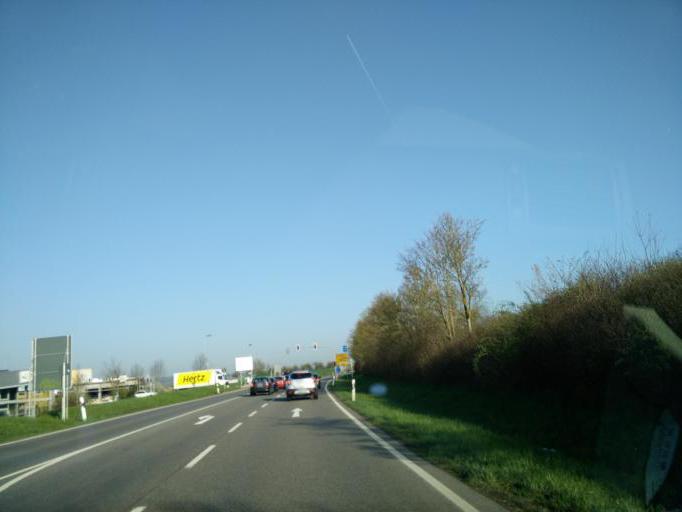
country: DE
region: Baden-Wuerttemberg
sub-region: Regierungsbezirk Stuttgart
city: Herrenberg
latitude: 48.5820
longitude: 8.8948
